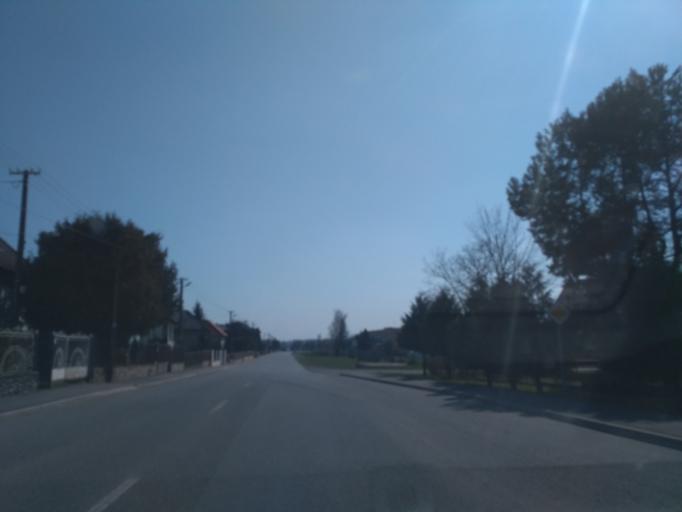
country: SK
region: Kosicky
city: Secovce
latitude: 48.6635
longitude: 21.6112
